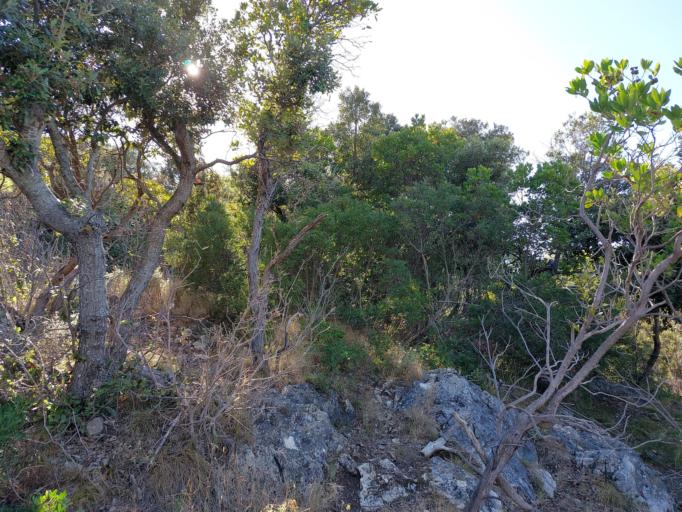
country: HR
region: Dubrovacko-Neretvanska
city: Smokvica
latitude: 42.7405
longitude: 16.8285
